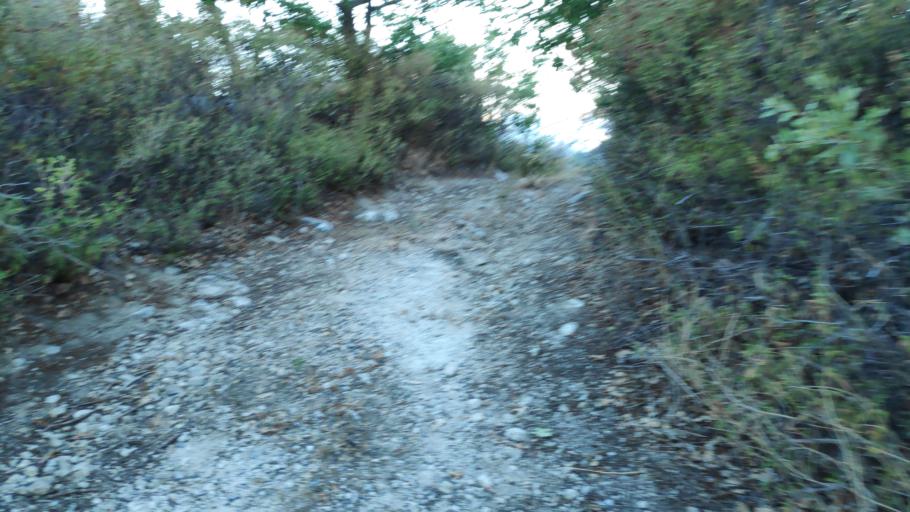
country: IT
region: Calabria
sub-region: Provincia di Reggio Calabria
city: Stilo
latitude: 38.4951
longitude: 16.4672
